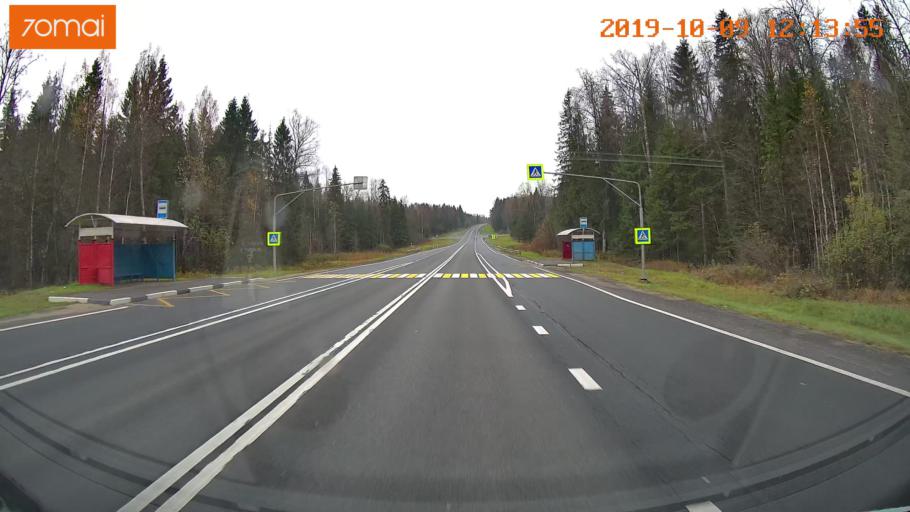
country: RU
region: Jaroslavl
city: Prechistoye
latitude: 58.5032
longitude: 40.3426
